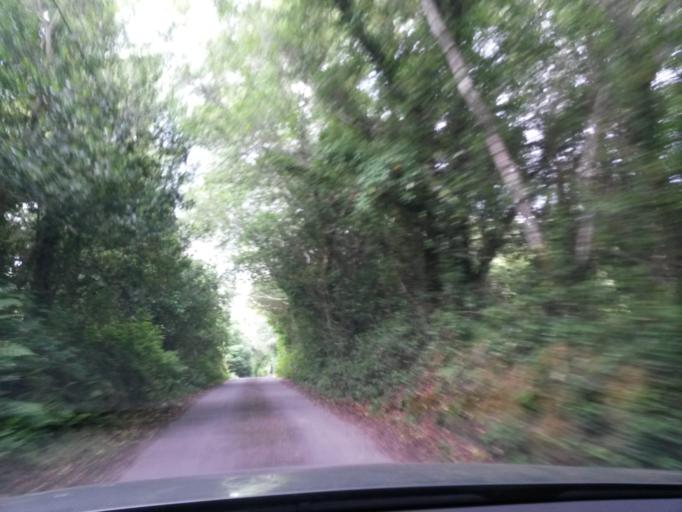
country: IE
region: Munster
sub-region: Ciarrai
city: Kenmare
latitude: 51.8303
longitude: -9.5212
